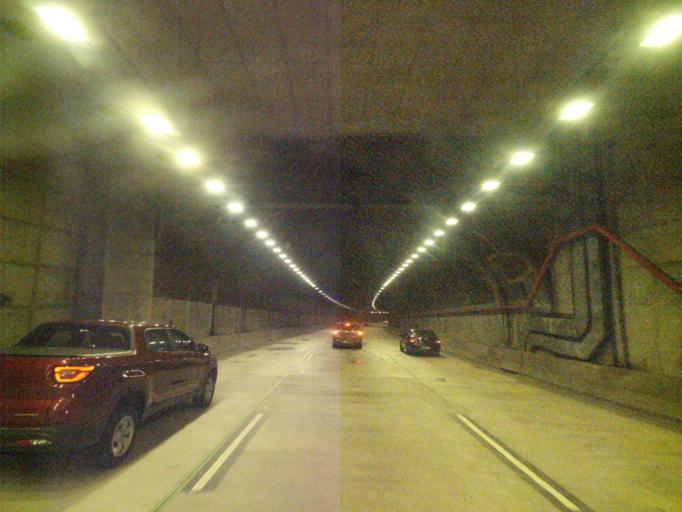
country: BR
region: Rio de Janeiro
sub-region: Rio De Janeiro
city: Rio de Janeiro
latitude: -22.8928
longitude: -43.1936
